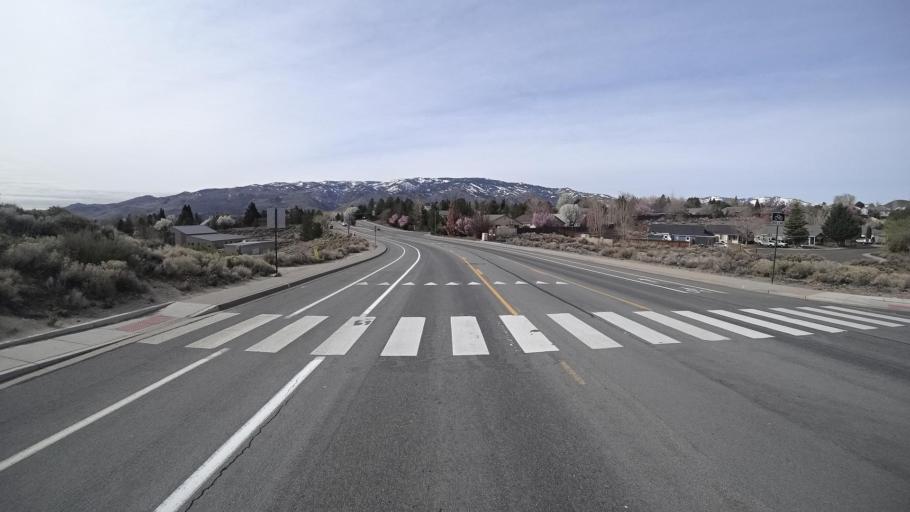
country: US
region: Nevada
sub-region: Washoe County
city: Mogul
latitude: 39.5270
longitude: -119.8947
